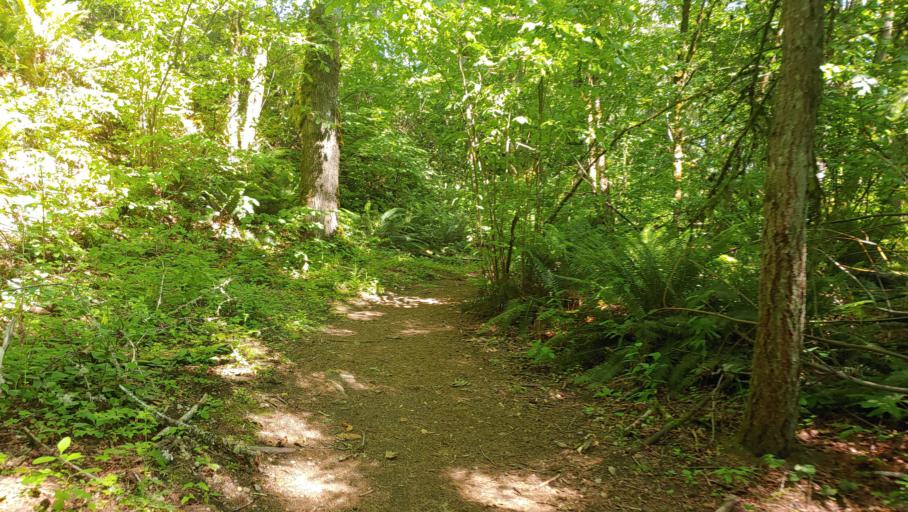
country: US
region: Washington
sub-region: King County
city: Newcastle
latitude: 47.5218
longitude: -122.1685
